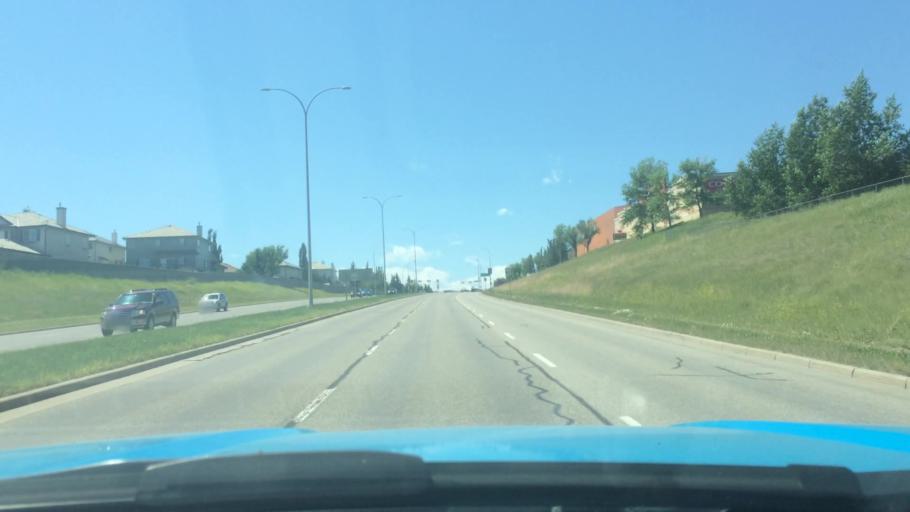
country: CA
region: Alberta
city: Calgary
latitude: 51.1416
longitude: -114.1277
